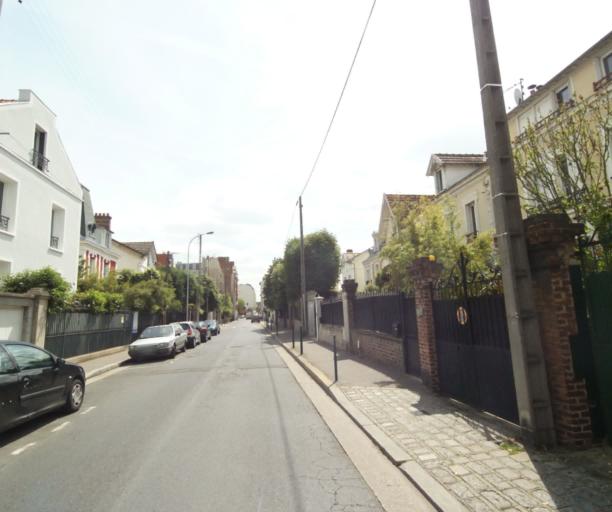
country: FR
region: Ile-de-France
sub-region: Departement des Hauts-de-Seine
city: Colombes
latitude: 48.9159
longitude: 2.2617
